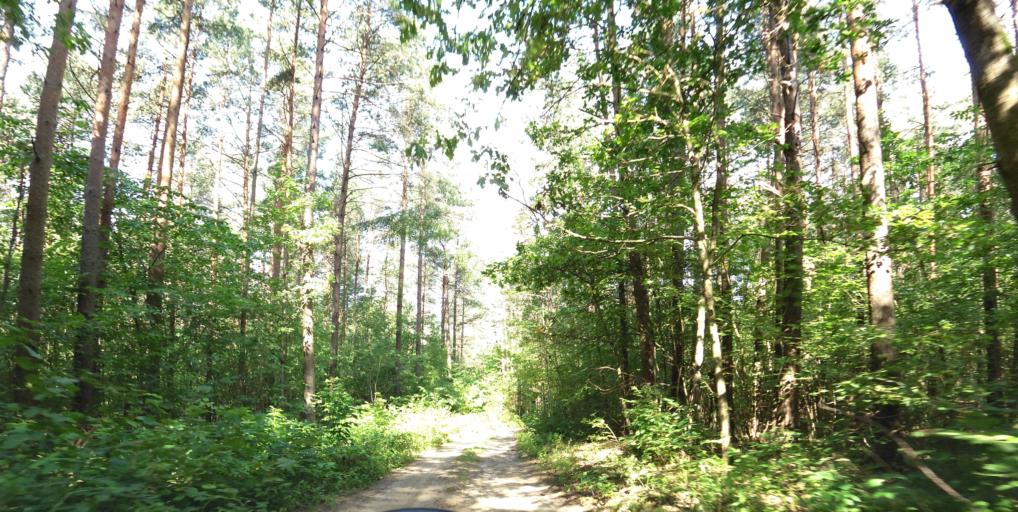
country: LT
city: Grigiskes
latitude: 54.7420
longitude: 25.0238
